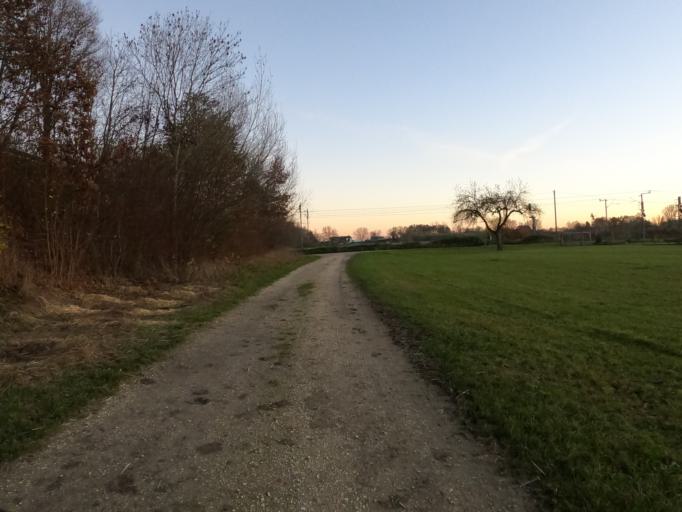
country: DE
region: Bavaria
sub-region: Swabia
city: Nersingen
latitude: 48.4272
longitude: 10.1091
